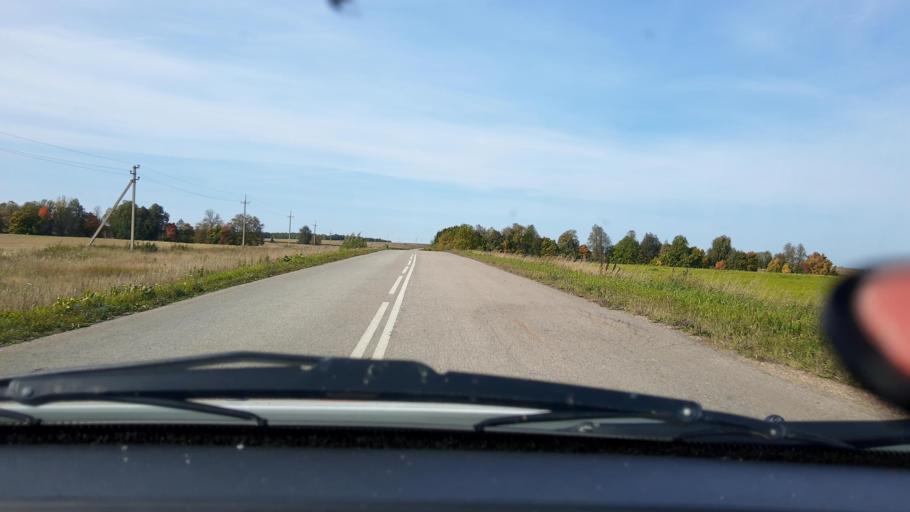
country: RU
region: Bashkortostan
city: Iglino
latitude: 54.7607
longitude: 56.5651
